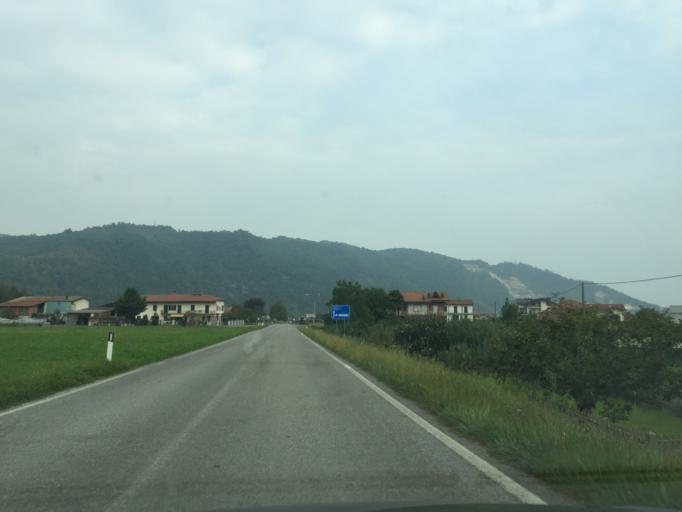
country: IT
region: Piedmont
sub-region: Provincia di Cuneo
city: Roccaforte Mondovi
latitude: 44.3106
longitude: 7.7448
